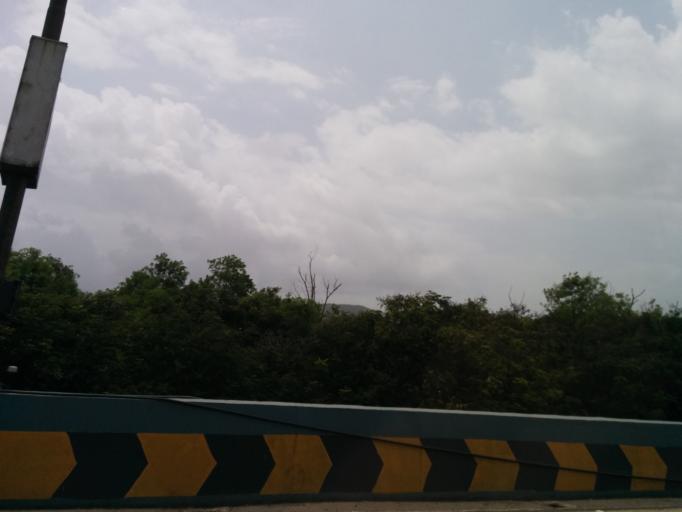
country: IN
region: Maharashtra
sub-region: Thane
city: Thane
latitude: 19.2051
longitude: 72.9694
